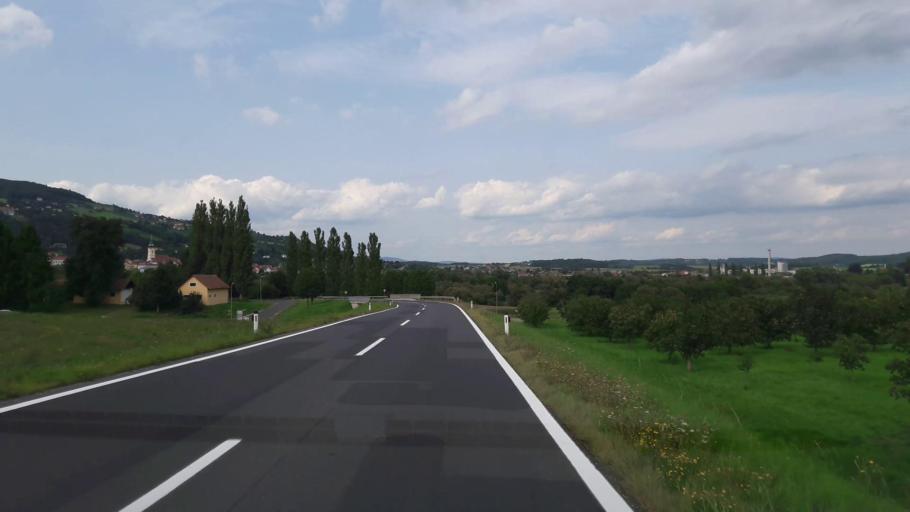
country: AT
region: Styria
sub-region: Politischer Bezirk Hartberg-Fuerstenfeld
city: Hartberg
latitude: 47.2684
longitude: 15.9708
